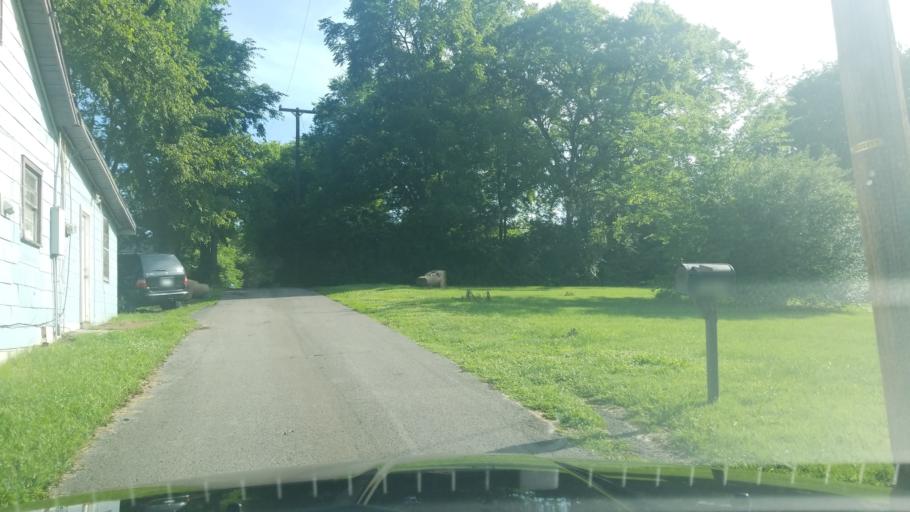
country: US
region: Tennessee
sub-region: Davidson County
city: Oak Hill
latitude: 36.1161
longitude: -86.7414
